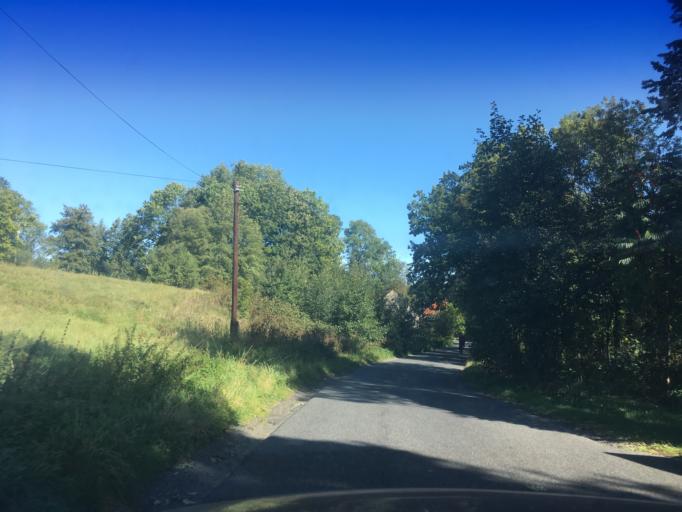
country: PL
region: Lower Silesian Voivodeship
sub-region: Powiat lubanski
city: Lesna
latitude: 51.0267
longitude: 15.2193
